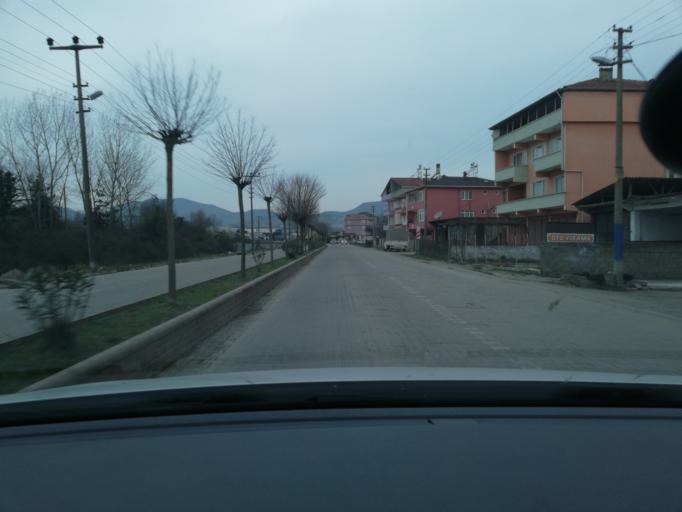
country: TR
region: Zonguldak
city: Caycuma
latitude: 41.4155
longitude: 32.0974
